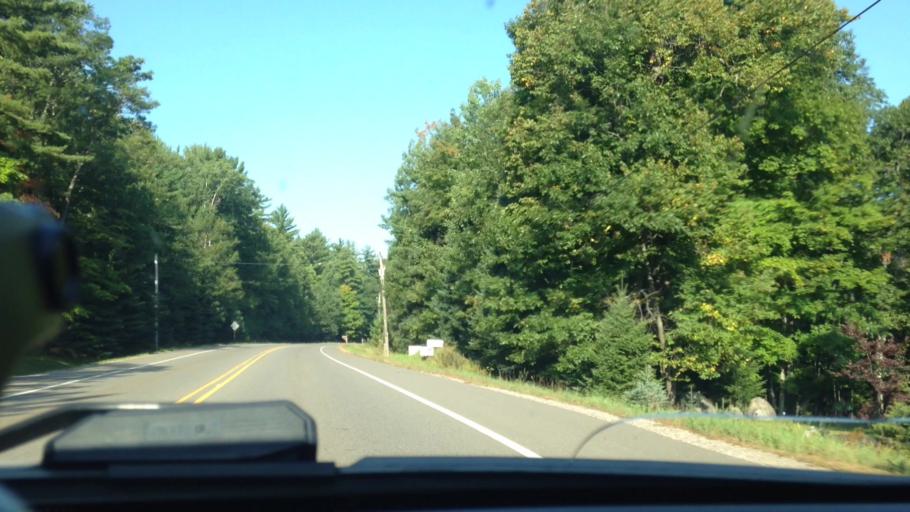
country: US
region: Michigan
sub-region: Dickinson County
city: Quinnesec
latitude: 45.8310
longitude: -88.0002
